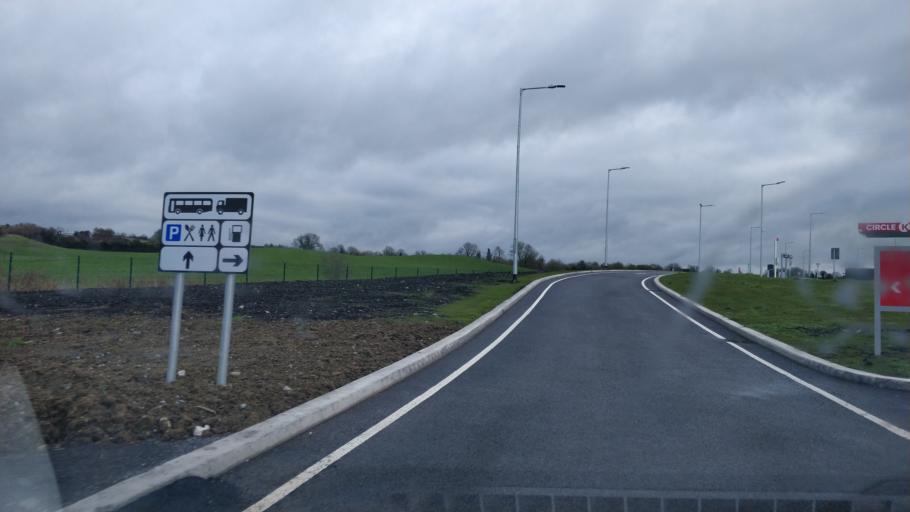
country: IE
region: Leinster
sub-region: An Iarmhi
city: Moate
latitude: 53.4014
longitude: -7.8289
